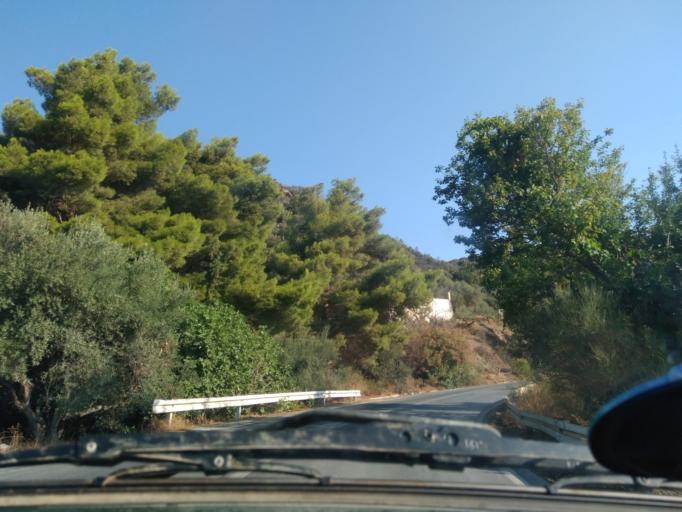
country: GR
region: Crete
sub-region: Nomos Lasithiou
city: Makry-Gialos
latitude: 35.1631
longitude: 25.9686
